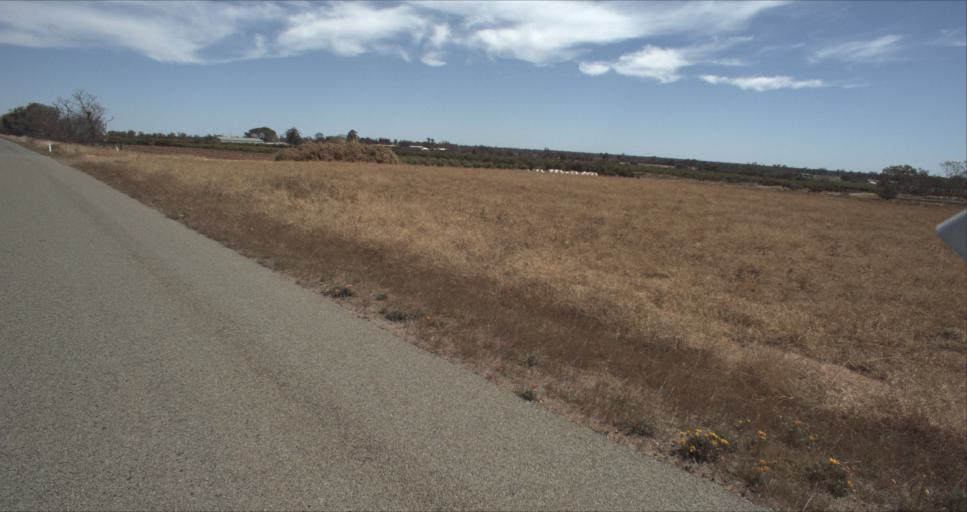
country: AU
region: New South Wales
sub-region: Leeton
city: Leeton
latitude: -34.6096
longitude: 146.4348
